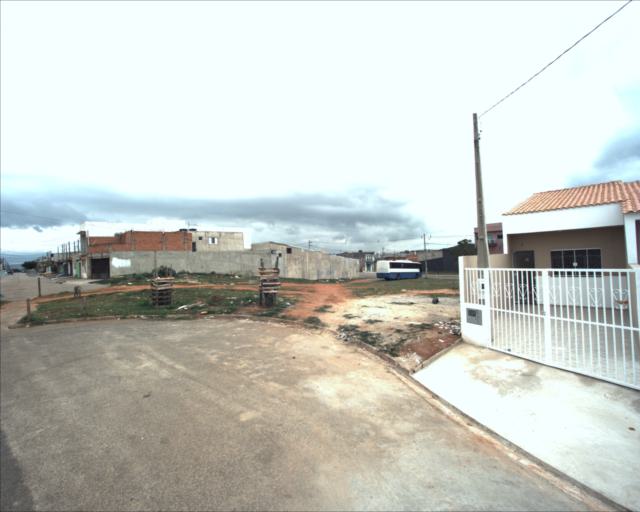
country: BR
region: Sao Paulo
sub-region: Sorocaba
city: Sorocaba
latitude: -23.4320
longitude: -47.5044
